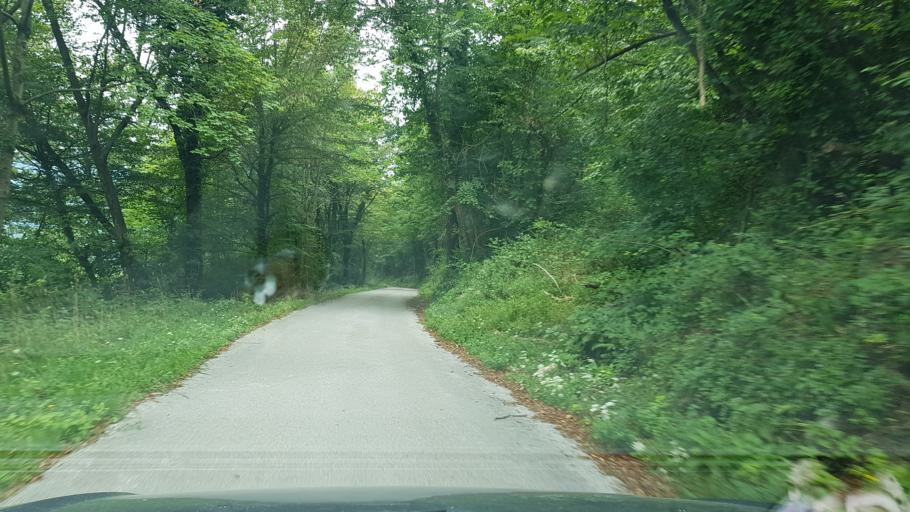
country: SI
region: Kanal
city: Deskle
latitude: 46.0262
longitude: 13.6135
